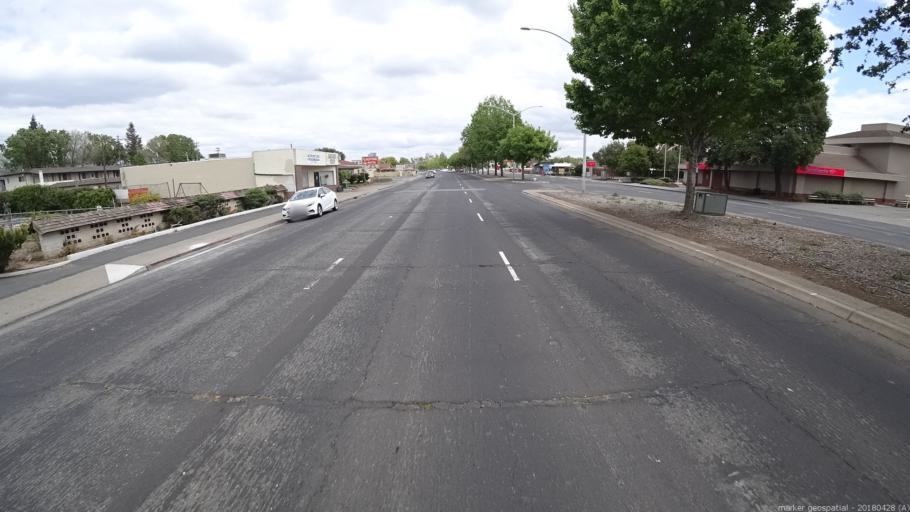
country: US
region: California
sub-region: Yolo County
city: West Sacramento
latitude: 38.5804
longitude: -121.5291
